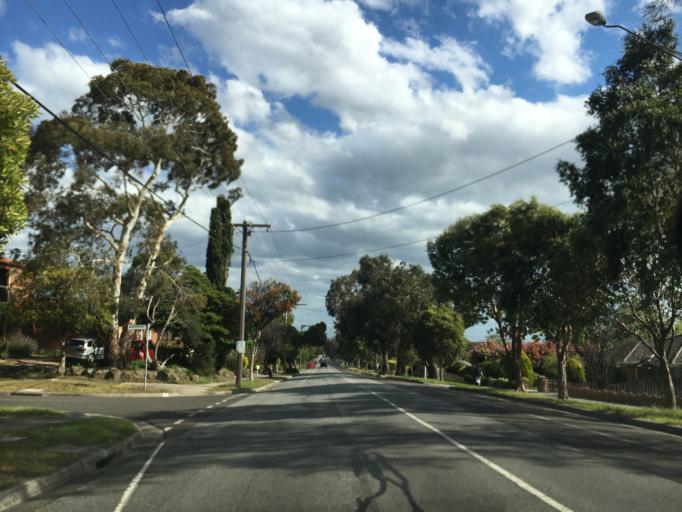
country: AU
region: Victoria
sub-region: Monash
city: Notting Hill
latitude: -37.8915
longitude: 145.1700
